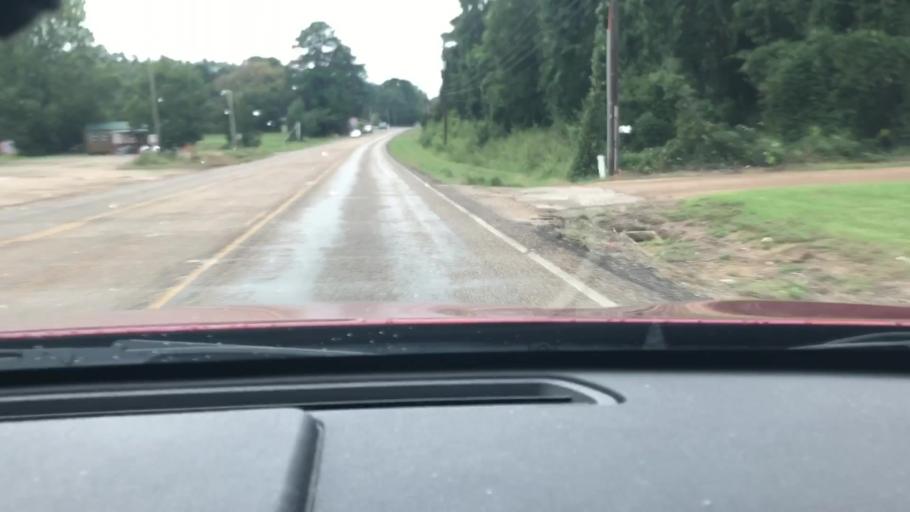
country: US
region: Texas
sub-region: Bowie County
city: Wake Village
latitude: 33.4438
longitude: -94.1115
